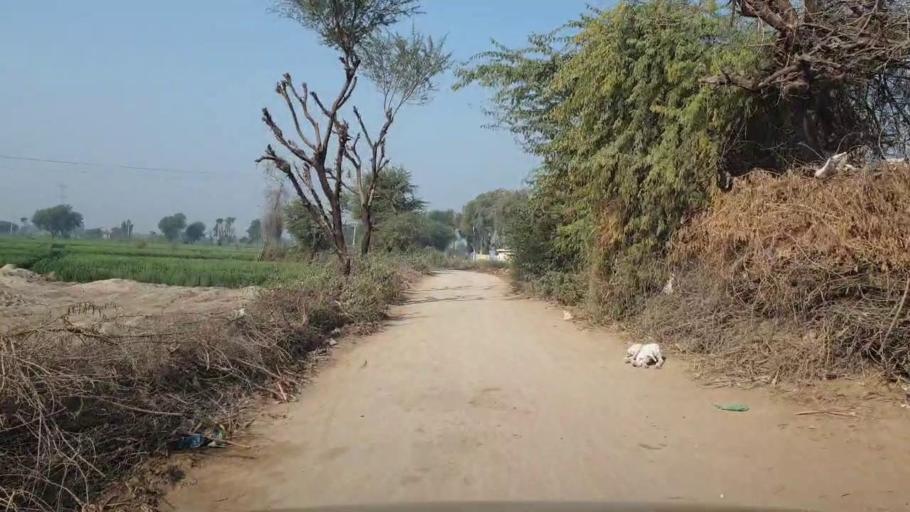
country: PK
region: Sindh
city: Matiari
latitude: 25.6764
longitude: 68.5000
